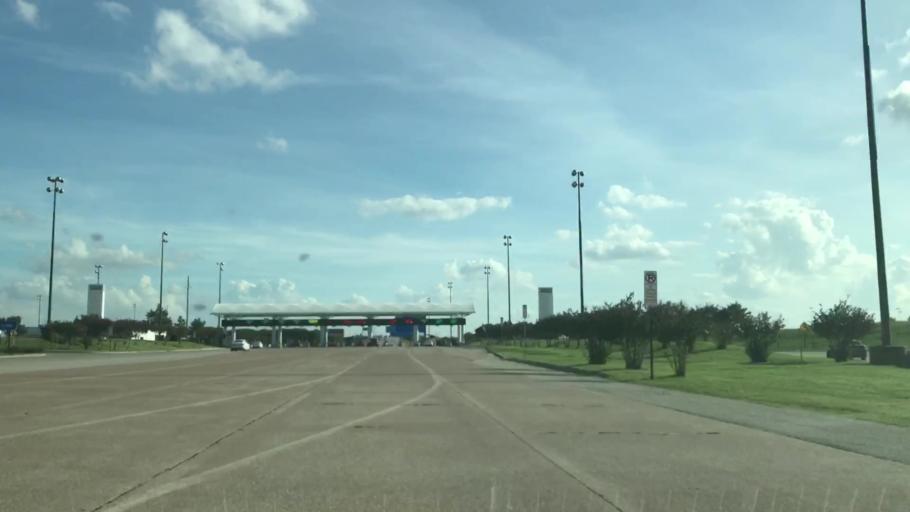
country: US
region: Texas
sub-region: Tarrant County
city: Grapevine
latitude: 32.9243
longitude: -97.0409
